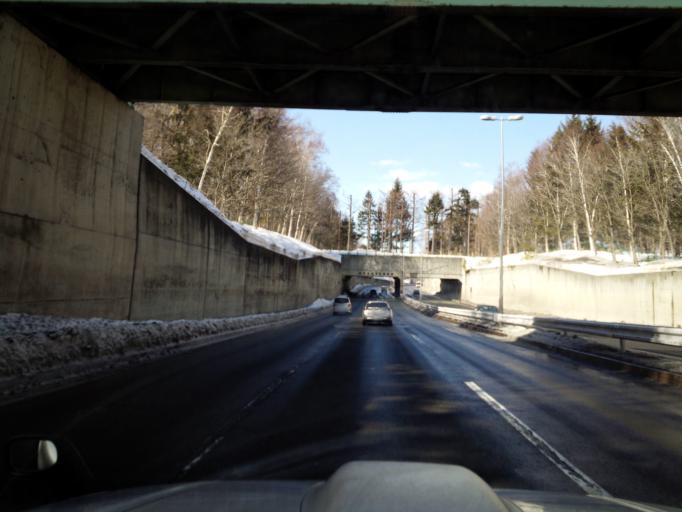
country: JP
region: Hokkaido
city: Sapporo
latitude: 43.0064
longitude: 141.4188
